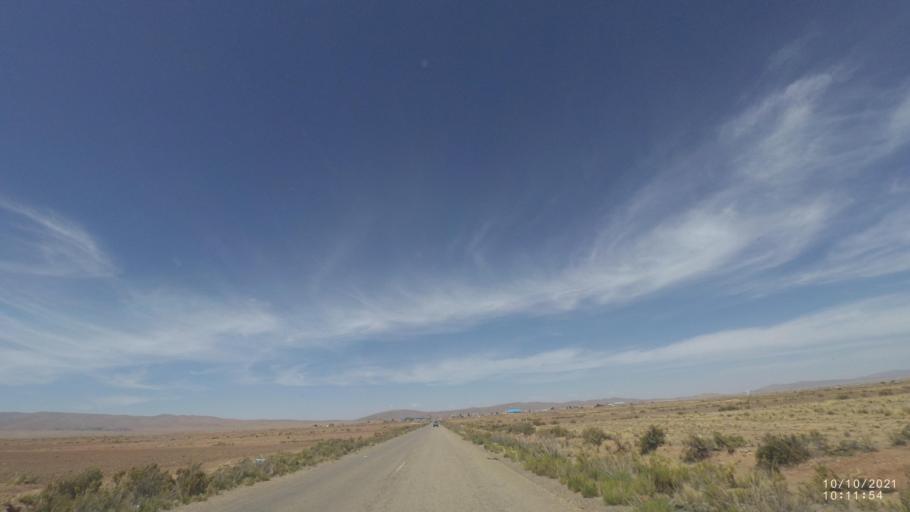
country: BO
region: La Paz
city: Eucaliptus
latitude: -17.4290
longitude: -67.5092
